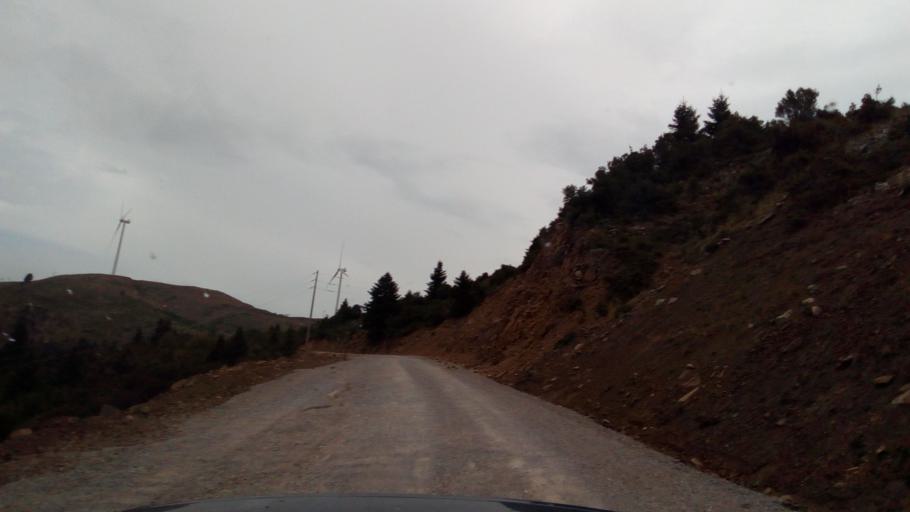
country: GR
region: Central Greece
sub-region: Nomos Fokidos
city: Lidoriki
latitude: 38.4478
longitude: 22.0732
